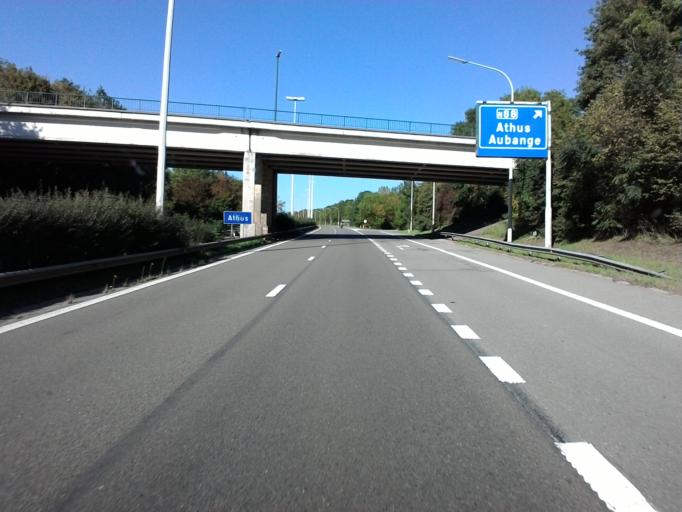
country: BE
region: Wallonia
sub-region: Province du Luxembourg
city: Aubange
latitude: 49.5631
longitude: 5.8188
